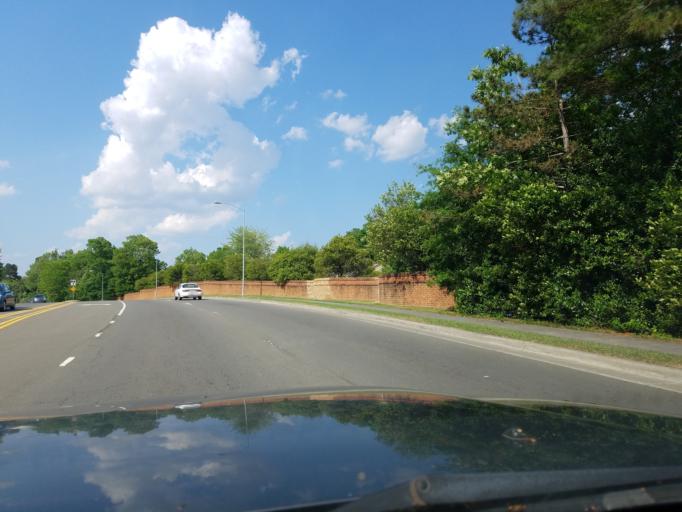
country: US
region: North Carolina
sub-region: Durham County
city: Durham
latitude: 35.9508
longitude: -78.9666
